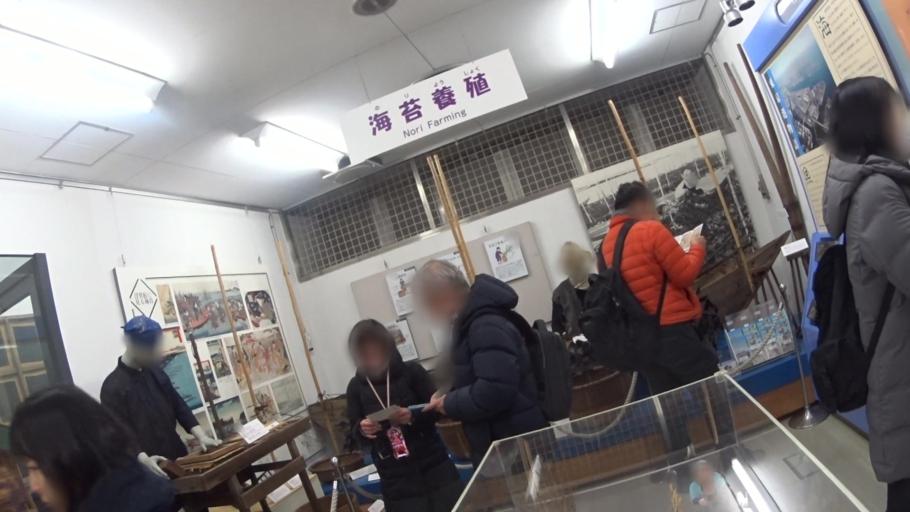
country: JP
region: Kanagawa
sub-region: Kawasaki-shi
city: Kawasaki
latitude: 35.5875
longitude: 139.7106
